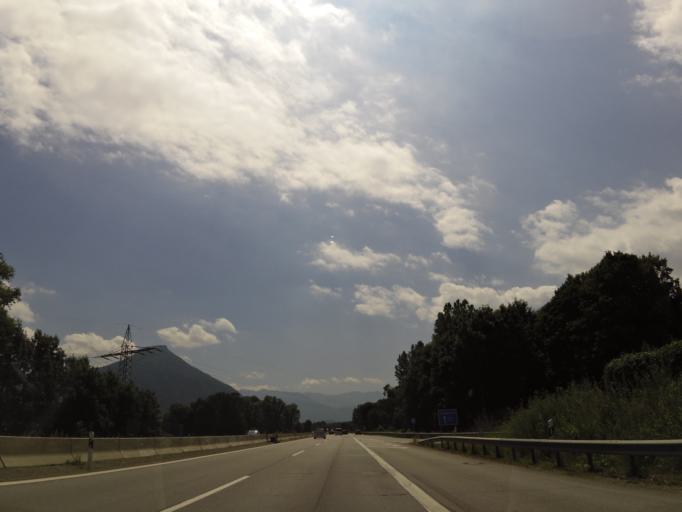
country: DE
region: Bavaria
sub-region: Upper Bavaria
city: Flintsbach
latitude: 47.7327
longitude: 12.1319
